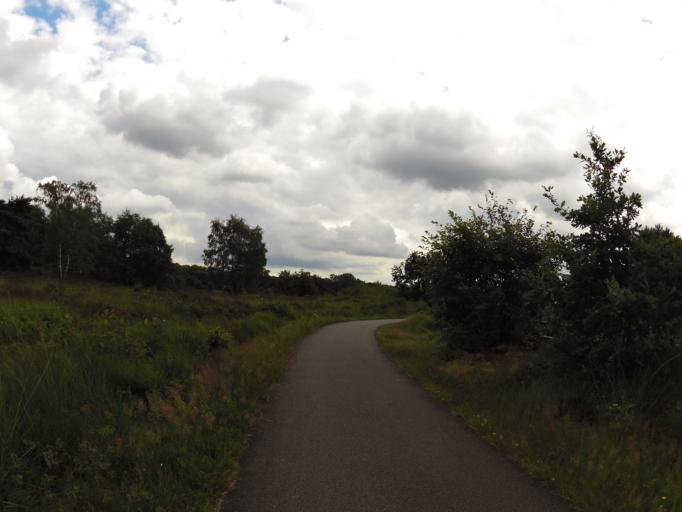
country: NL
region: North Brabant
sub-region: Gemeente Valkenswaard
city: Valkenswaard
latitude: 51.3218
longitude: 5.4540
